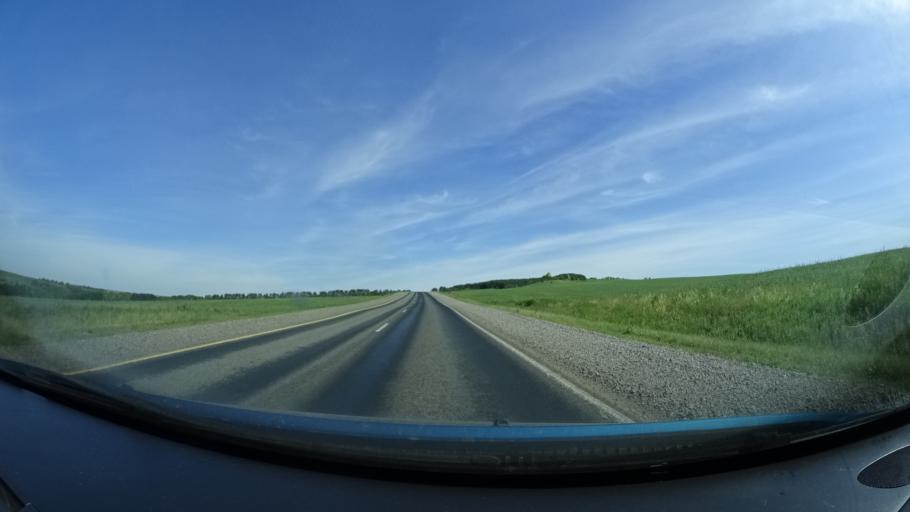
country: RU
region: Bashkortostan
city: Blagoveshchensk
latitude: 55.1251
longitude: 55.8424
